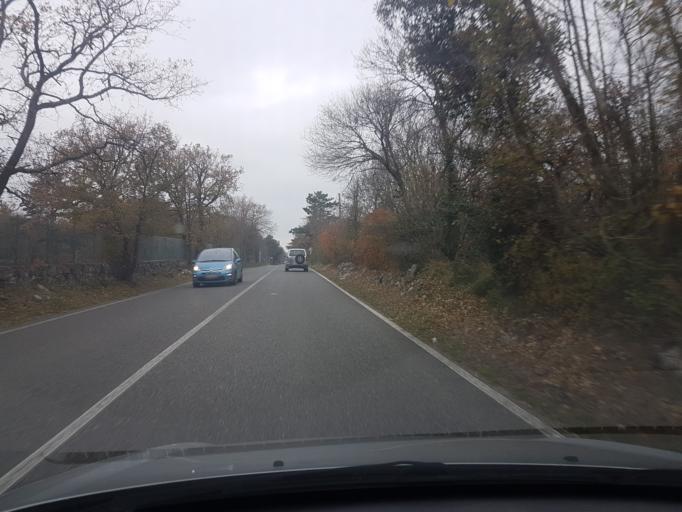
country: IT
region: Friuli Venezia Giulia
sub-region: Provincia di Trieste
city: Prosecco-Contovello
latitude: 45.7212
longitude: 13.7194
